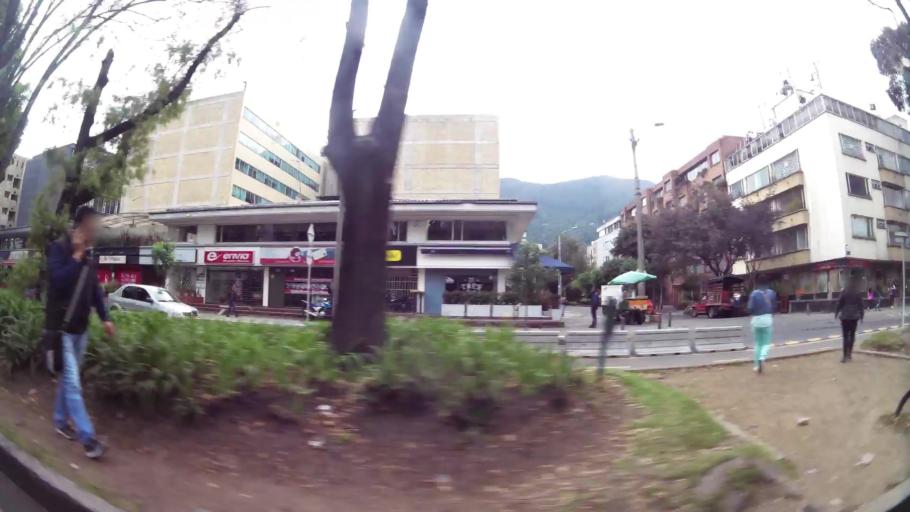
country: CO
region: Bogota D.C.
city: Barrio San Luis
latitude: 4.6806
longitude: -74.0442
